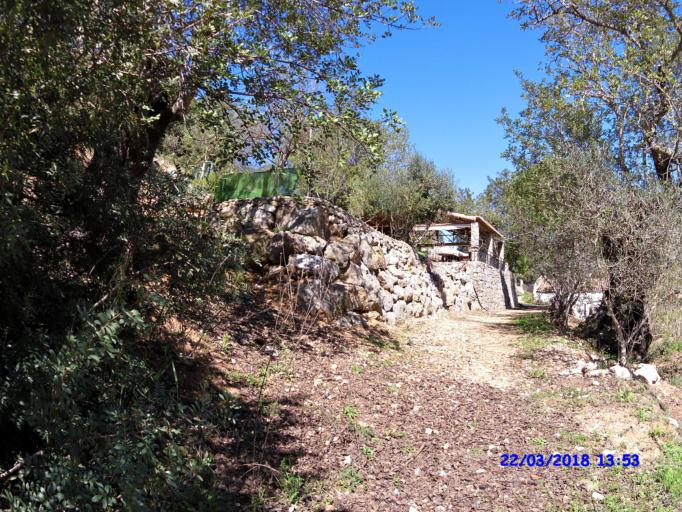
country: PT
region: Faro
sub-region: Albufeira
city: Ferreiras
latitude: 37.1570
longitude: -8.2025
